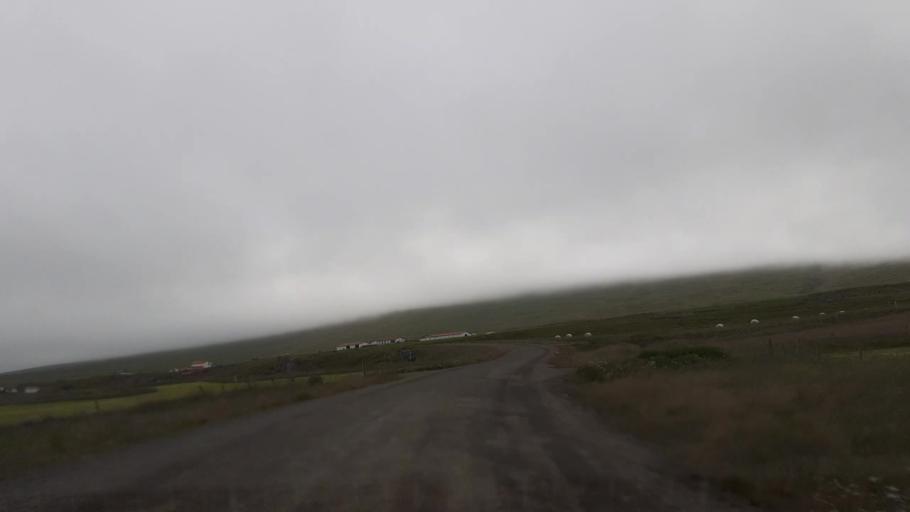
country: IS
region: Northwest
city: Saudarkrokur
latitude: 65.5298
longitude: -20.9589
